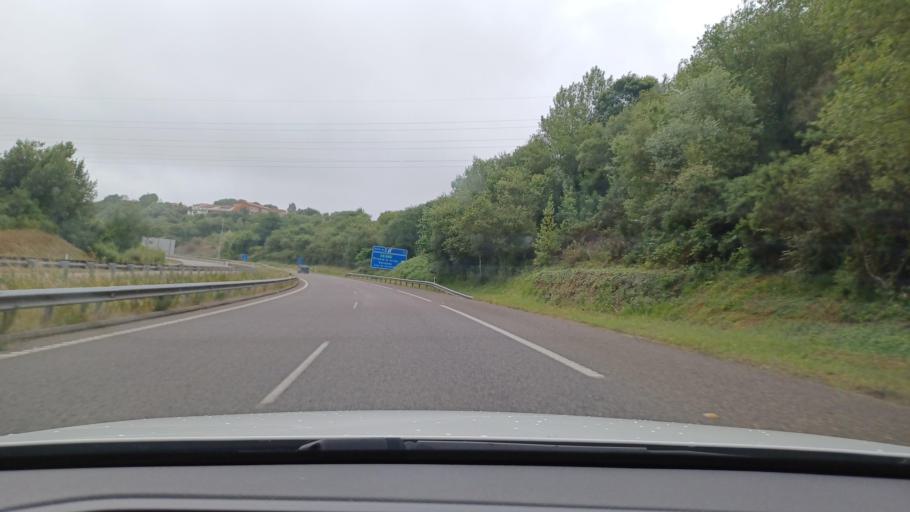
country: ES
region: Asturias
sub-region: Province of Asturias
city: Lugones
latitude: 43.4518
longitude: -5.7737
